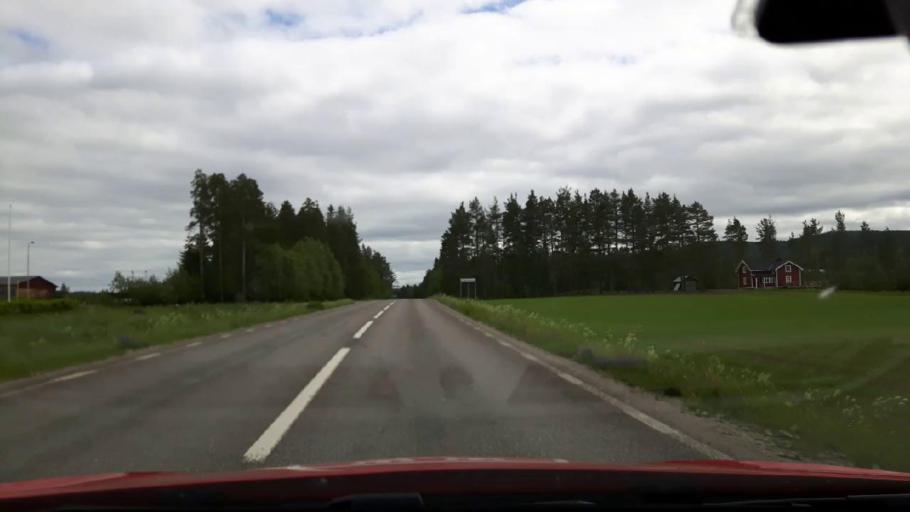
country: SE
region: Jaemtland
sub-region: Ragunda Kommun
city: Hammarstrand
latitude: 63.0878
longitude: 16.3627
